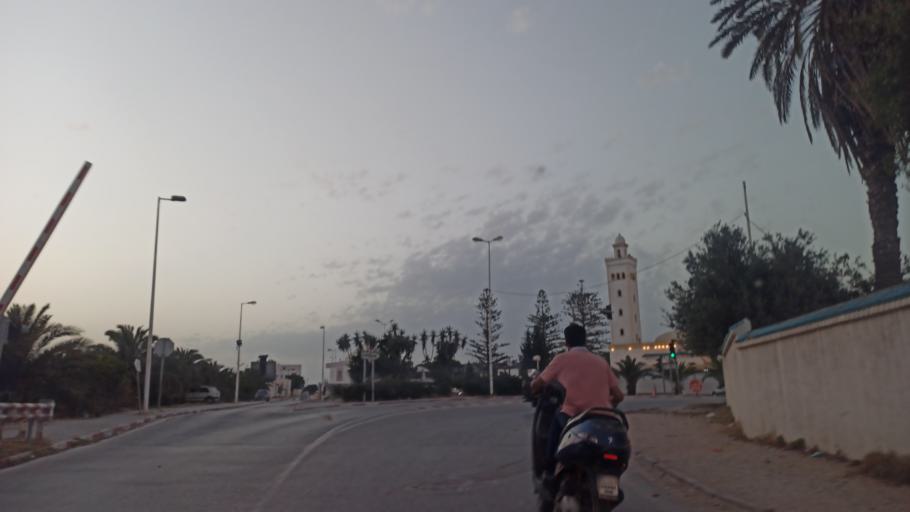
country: TN
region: Nabul
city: Al Hammamat
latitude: 36.4095
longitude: 10.6093
